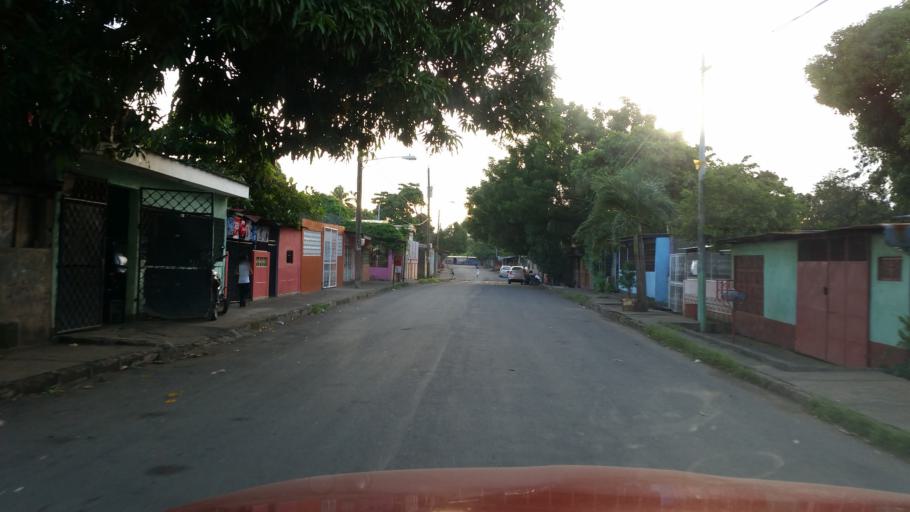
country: NI
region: Managua
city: Managua
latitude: 12.1271
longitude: -86.2898
